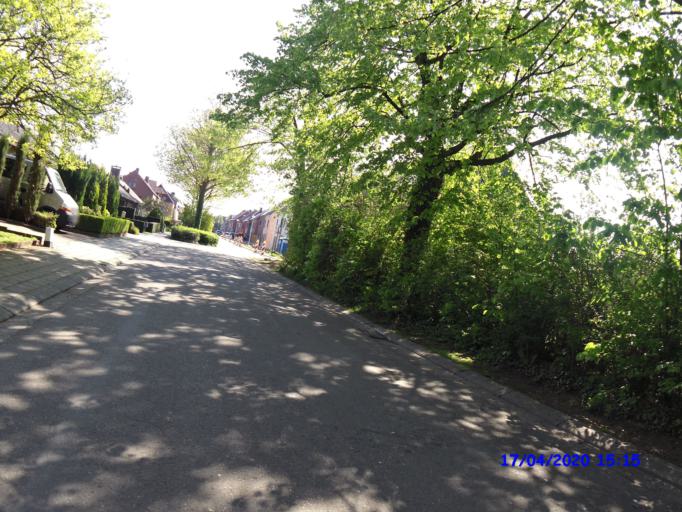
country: BE
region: Flanders
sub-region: Provincie Antwerpen
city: Turnhout
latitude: 51.3248
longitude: 4.9637
